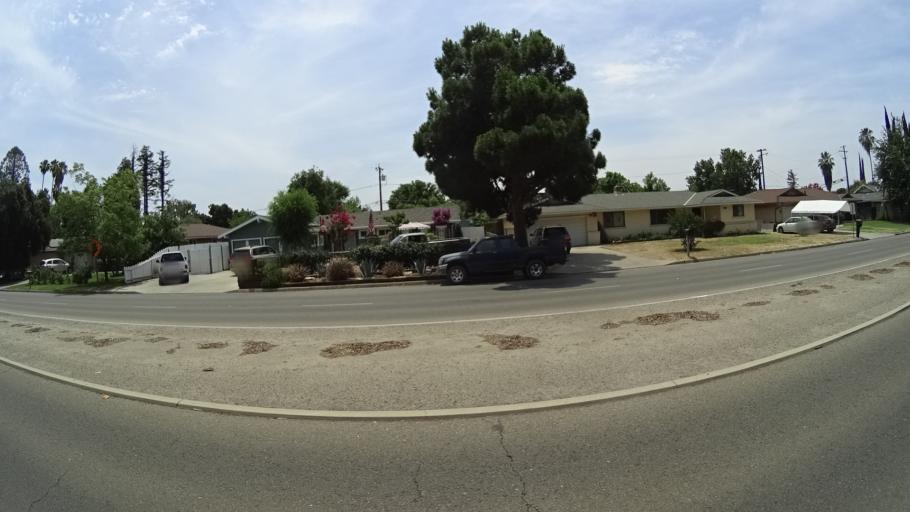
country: US
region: California
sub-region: Fresno County
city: Sunnyside
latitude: 36.7506
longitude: -119.7085
